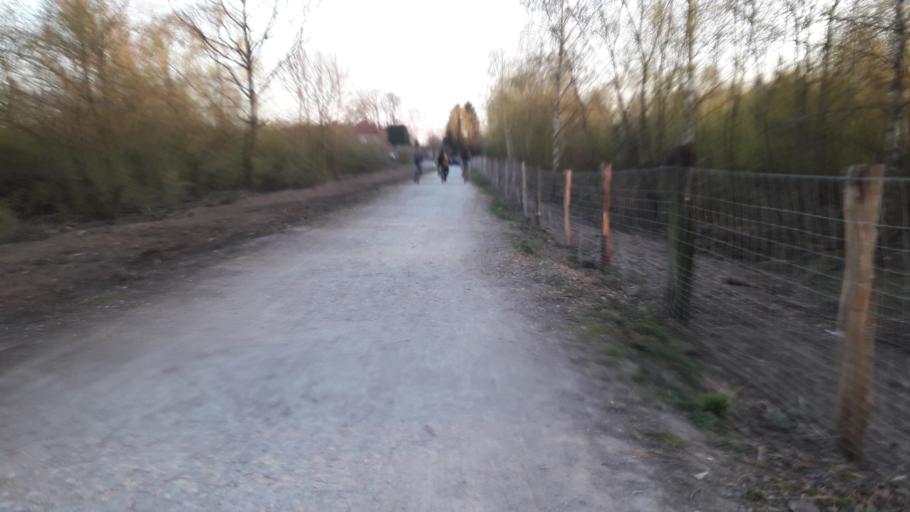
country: DE
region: North Rhine-Westphalia
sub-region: Regierungsbezirk Detmold
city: Hovelhof
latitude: 51.7531
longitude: 8.6883
